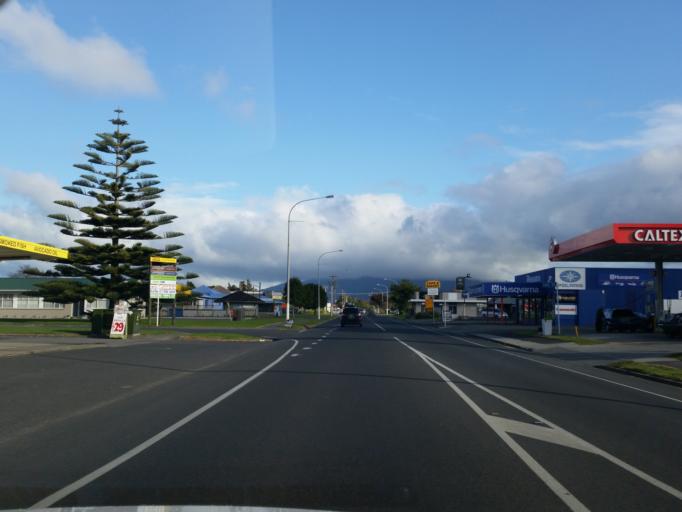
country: NZ
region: Bay of Plenty
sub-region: Western Bay of Plenty District
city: Katikati
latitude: -37.5574
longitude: 175.9167
